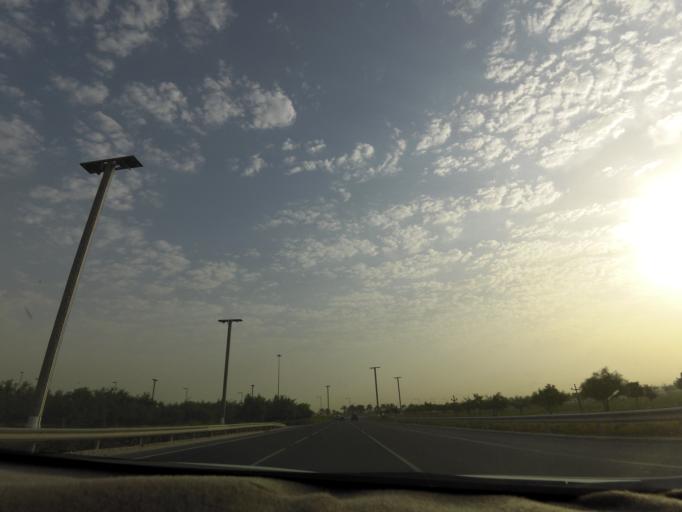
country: QA
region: Al Wakrah
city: Al Wakrah
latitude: 25.2393
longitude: 51.5942
